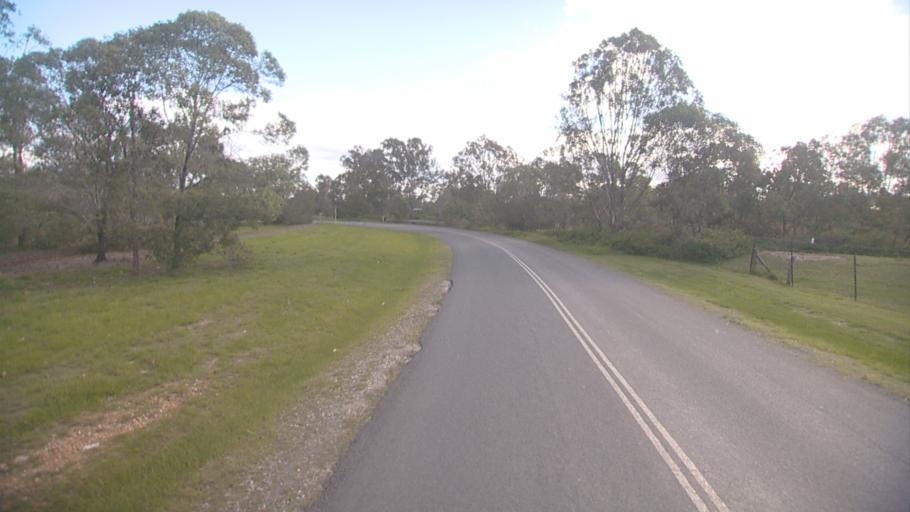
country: AU
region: Queensland
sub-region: Logan
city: Waterford West
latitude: -27.7021
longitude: 153.1484
